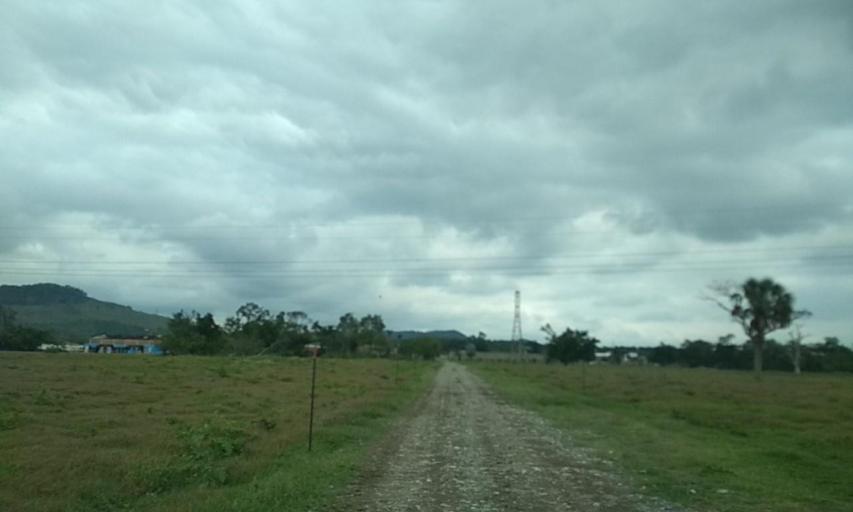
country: MX
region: Veracruz
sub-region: Papantla
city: El Chote
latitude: 20.3922
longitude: -97.3404
